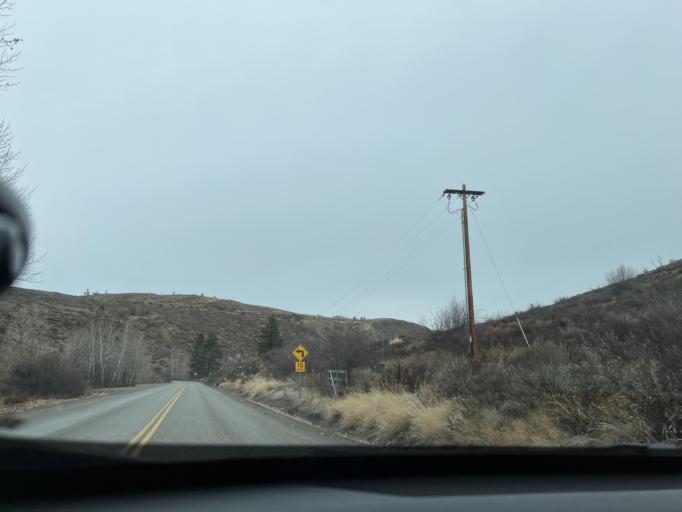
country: US
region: Washington
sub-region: Chelan County
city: Granite Falls
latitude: 48.4660
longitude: -120.2487
